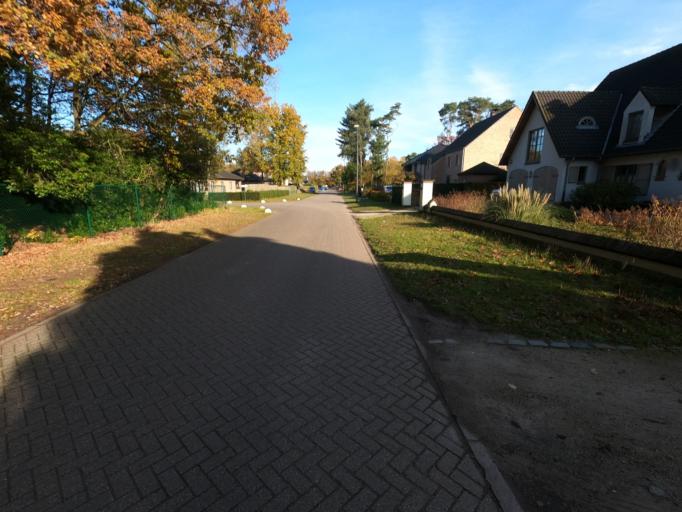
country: BE
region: Flanders
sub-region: Provincie Antwerpen
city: Wuustwezel
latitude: 51.3478
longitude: 4.5480
